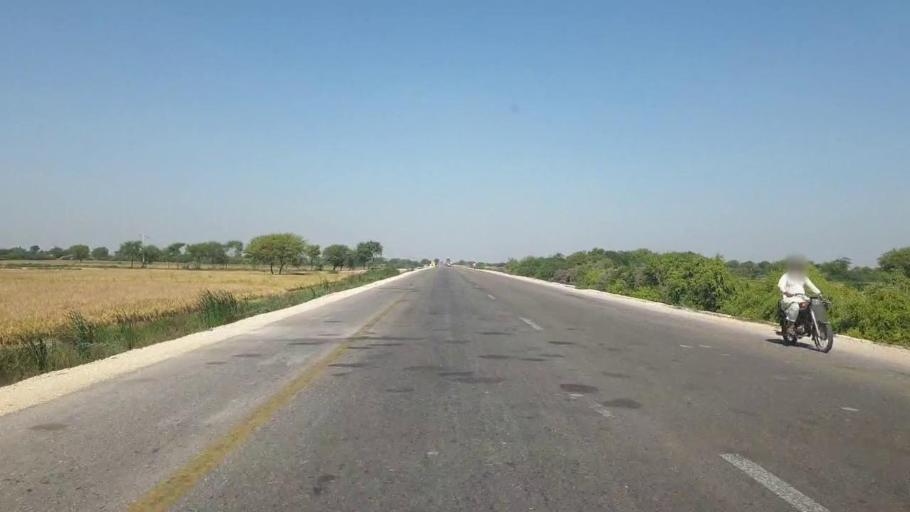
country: PK
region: Sindh
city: Talhar
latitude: 24.8231
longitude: 68.8159
